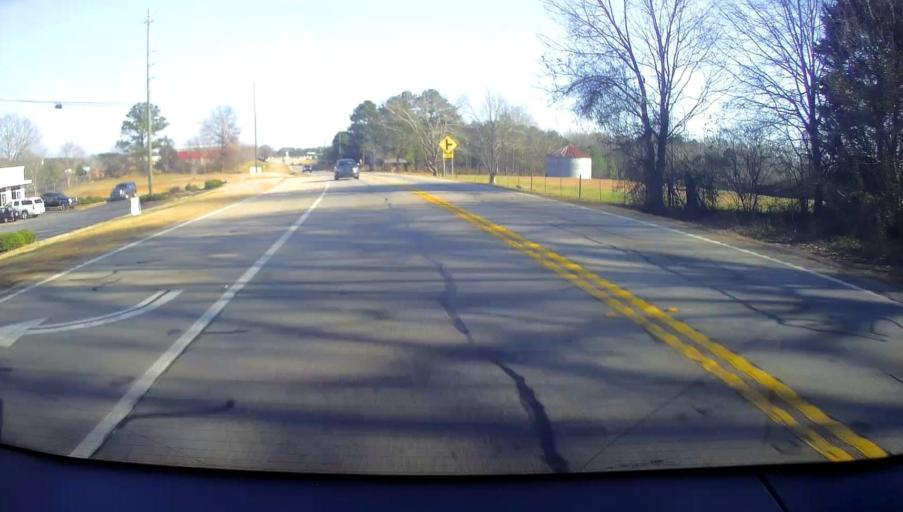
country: US
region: Georgia
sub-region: Henry County
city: Locust Grove
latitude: 33.3212
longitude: -84.0594
